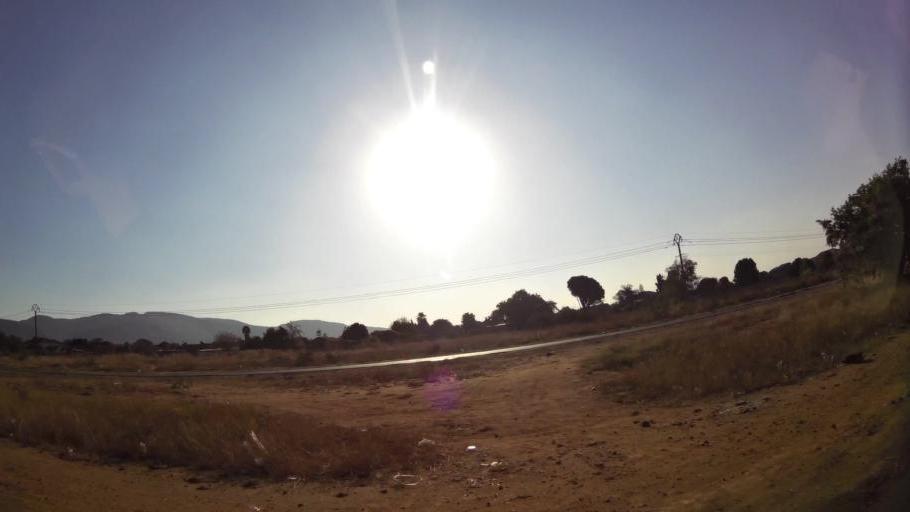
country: ZA
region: North-West
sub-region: Bojanala Platinum District Municipality
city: Rustenburg
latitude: -25.6523
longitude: 27.2215
